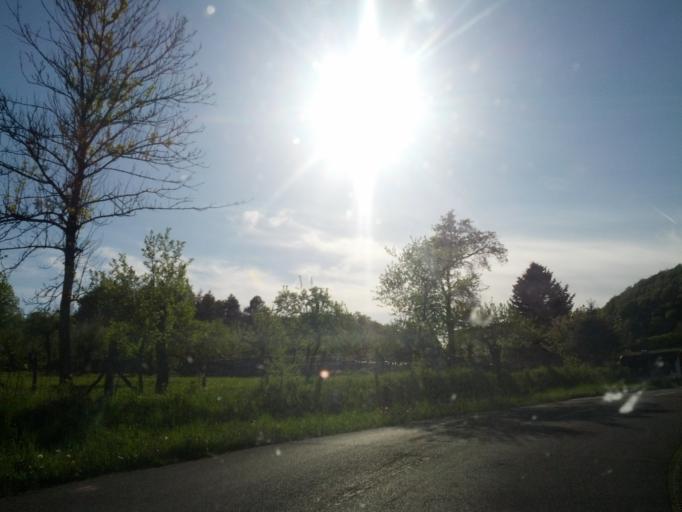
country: DE
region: Thuringia
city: Geismar
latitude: 51.2147
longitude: 10.1667
